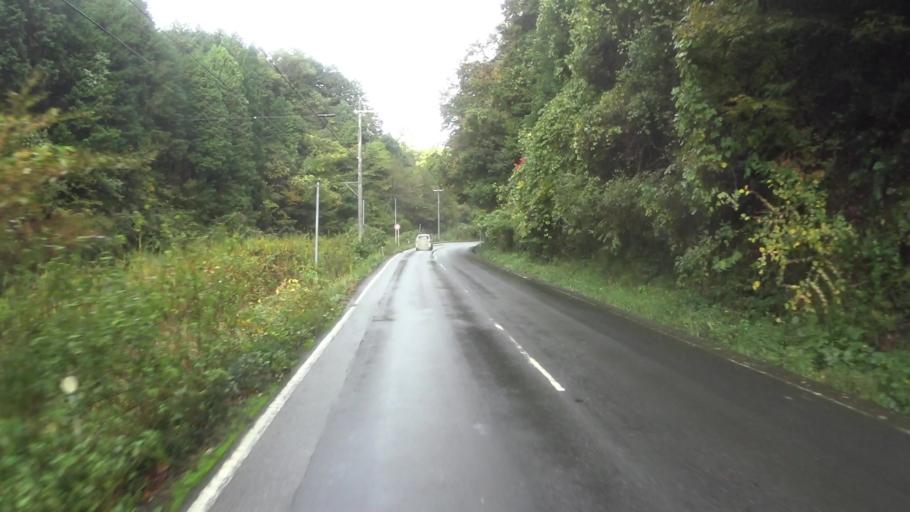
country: JP
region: Kyoto
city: Ayabe
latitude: 35.3777
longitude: 135.1839
